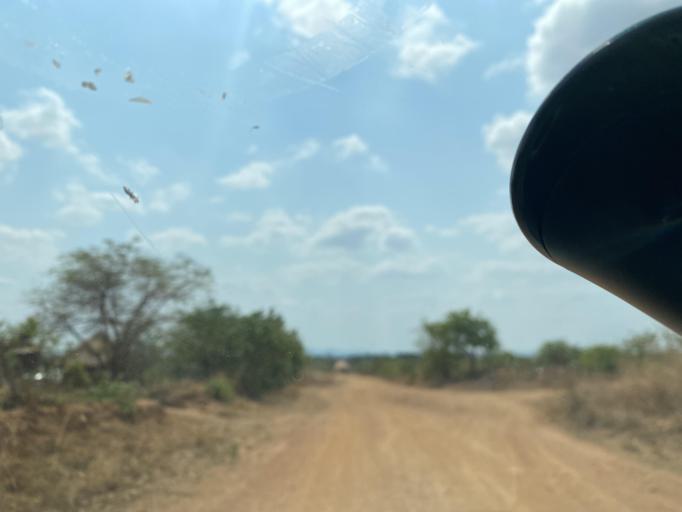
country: ZM
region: Lusaka
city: Chongwe
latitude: -15.5909
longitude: 28.7820
